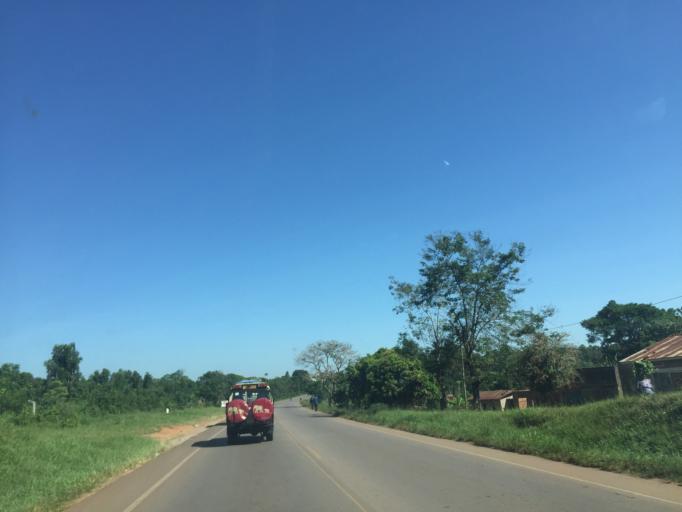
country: UG
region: Central Region
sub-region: Luwero District
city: Wobulenzi
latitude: 0.7575
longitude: 32.5140
